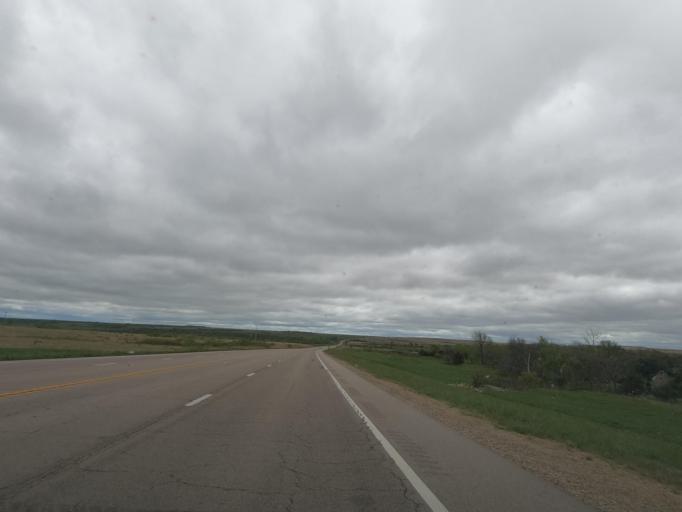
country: US
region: Kansas
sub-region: Greenwood County
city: Eureka
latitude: 37.6601
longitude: -96.4884
